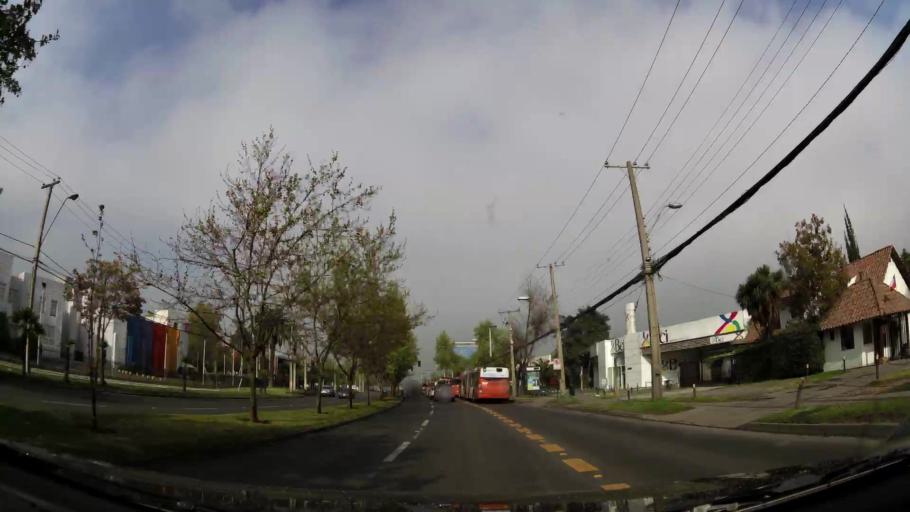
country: CL
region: Santiago Metropolitan
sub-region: Provincia de Santiago
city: Villa Presidente Frei, Nunoa, Santiago, Chile
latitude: -33.3774
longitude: -70.5277
